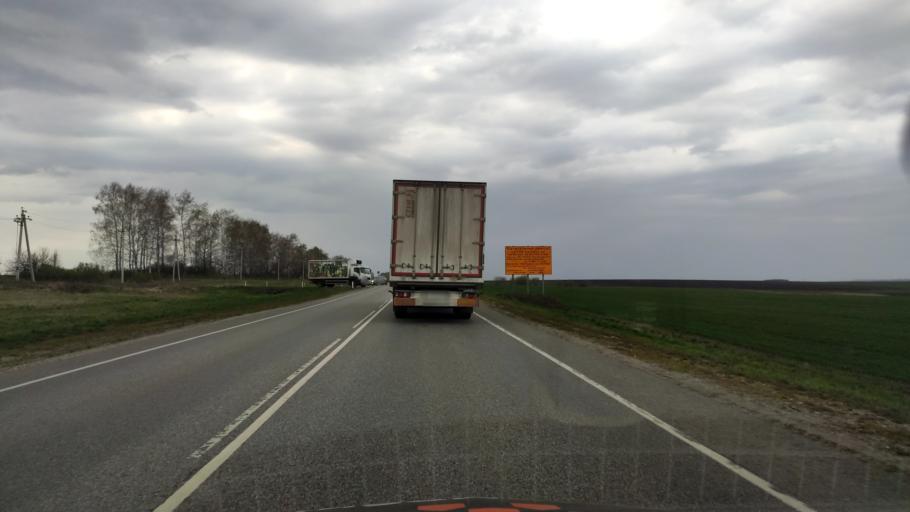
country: RU
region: Kursk
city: Gorshechnoye
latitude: 51.5487
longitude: 38.1188
